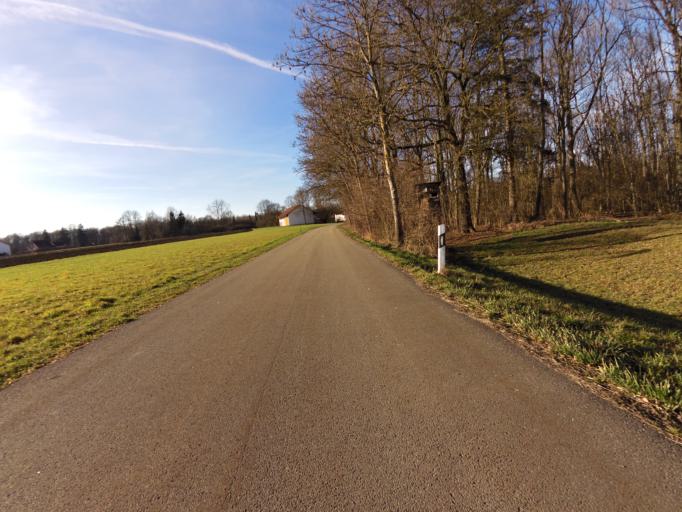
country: DE
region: Bavaria
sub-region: Upper Bavaria
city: Wang
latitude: 48.4976
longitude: 11.9617
